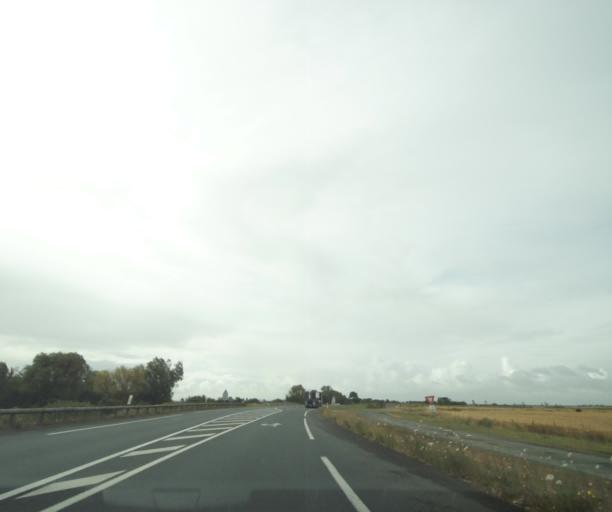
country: FR
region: Pays de la Loire
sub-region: Departement de la Vendee
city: Champagne-les-Marais
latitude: 46.4167
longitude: -1.1005
